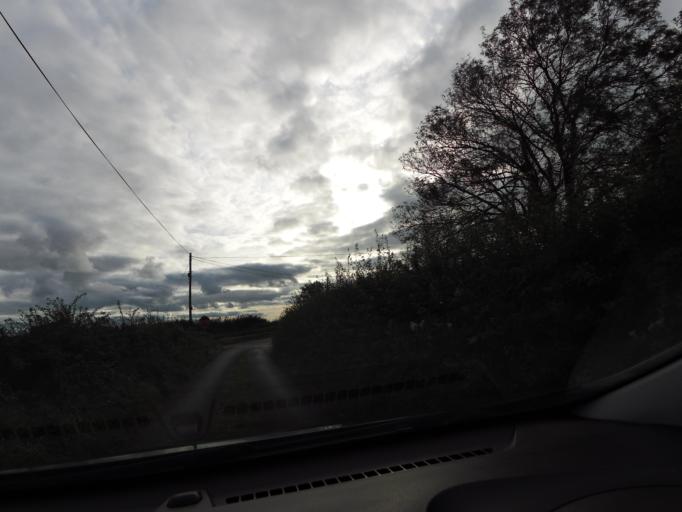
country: IE
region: Connaught
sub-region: County Galway
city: Ballinasloe
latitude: 53.3656
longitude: -8.1587
